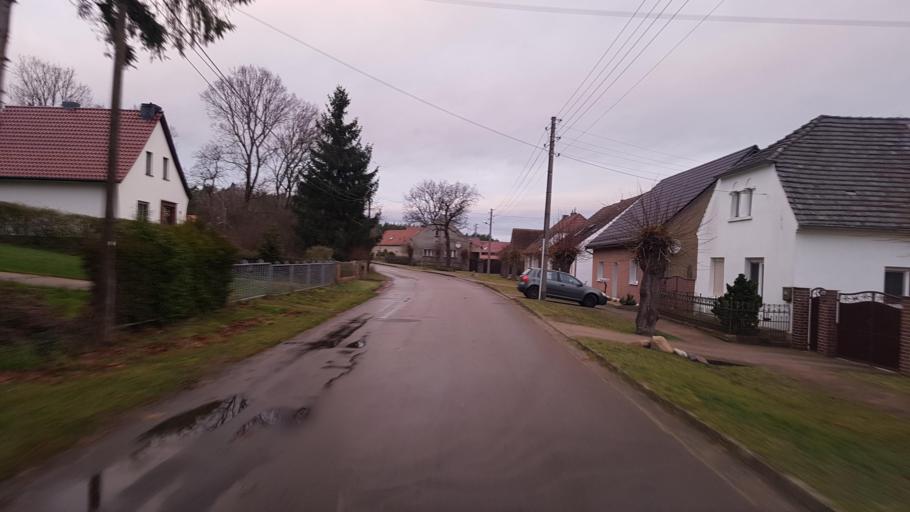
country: DE
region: Brandenburg
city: Luebben
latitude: 51.9067
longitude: 13.8083
